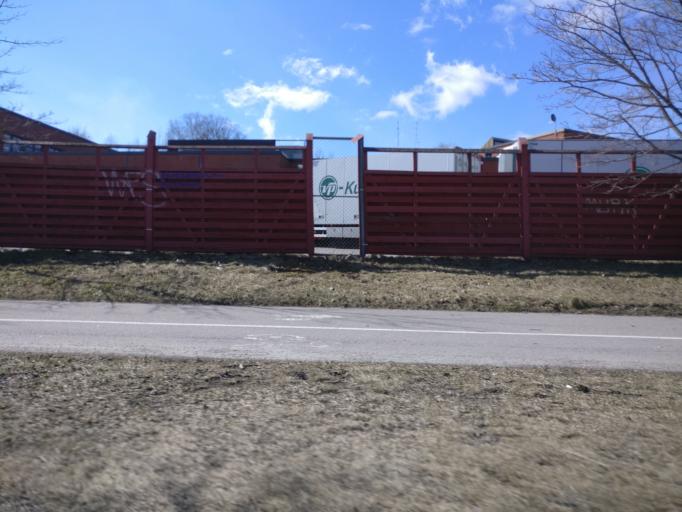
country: FI
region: Uusimaa
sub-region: Helsinki
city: Helsinki
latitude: 60.1938
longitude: 24.9772
